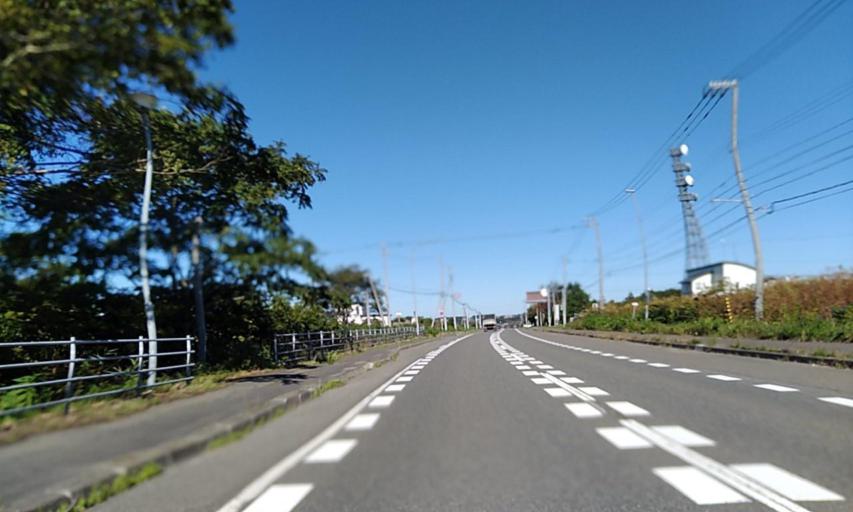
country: JP
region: Hokkaido
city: Shizunai-furukawacho
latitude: 42.5031
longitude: 142.0435
